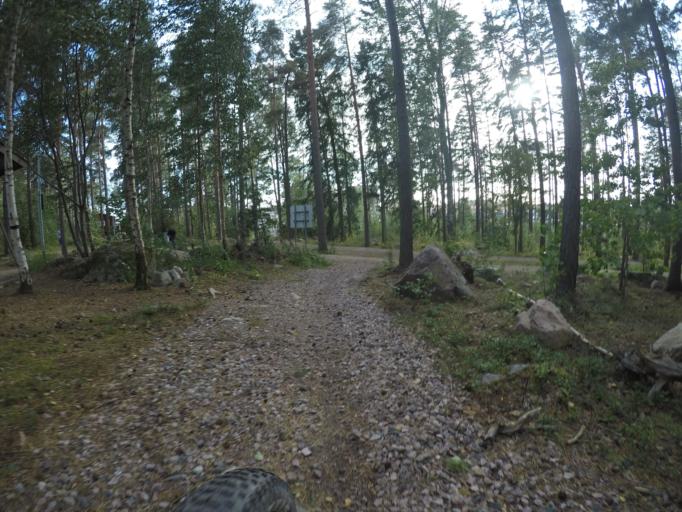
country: SE
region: Vaestmanland
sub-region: Kopings Kommun
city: Koping
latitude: 59.5256
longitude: 16.0002
